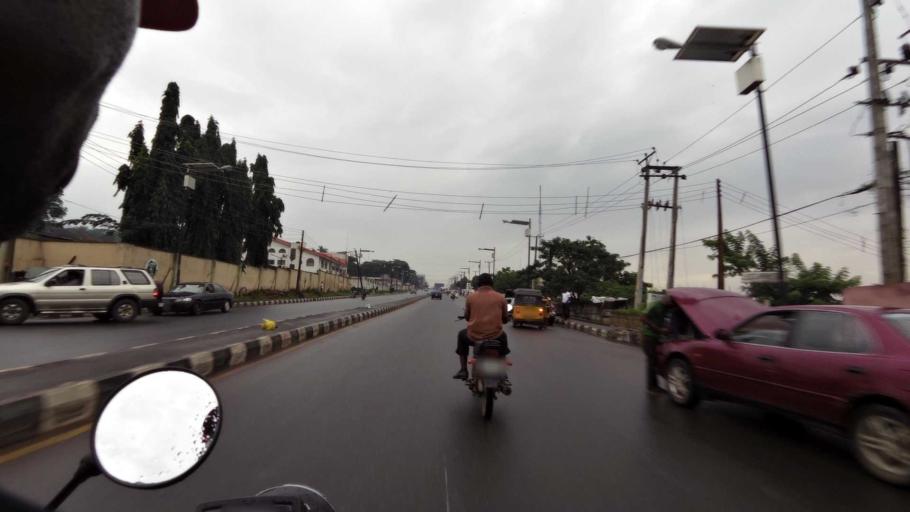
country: NG
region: Oyo
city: Ibadan
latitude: 7.3979
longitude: 3.9125
